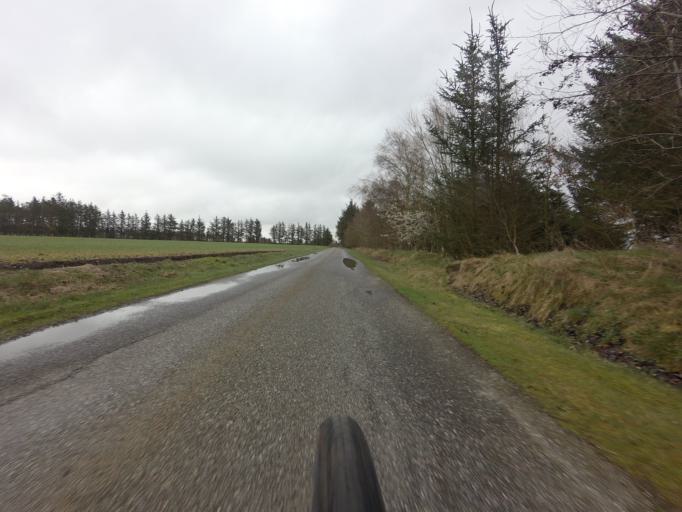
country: DK
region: North Denmark
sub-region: Bronderslev Kommune
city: Bronderslev
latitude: 57.3220
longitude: 9.7953
